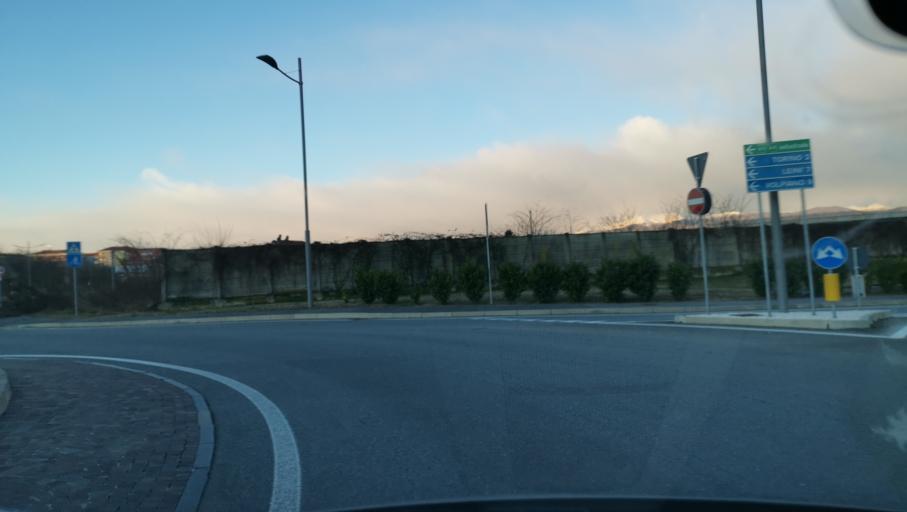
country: IT
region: Piedmont
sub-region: Provincia di Torino
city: Settimo Torinese
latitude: 45.1268
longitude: 7.7365
